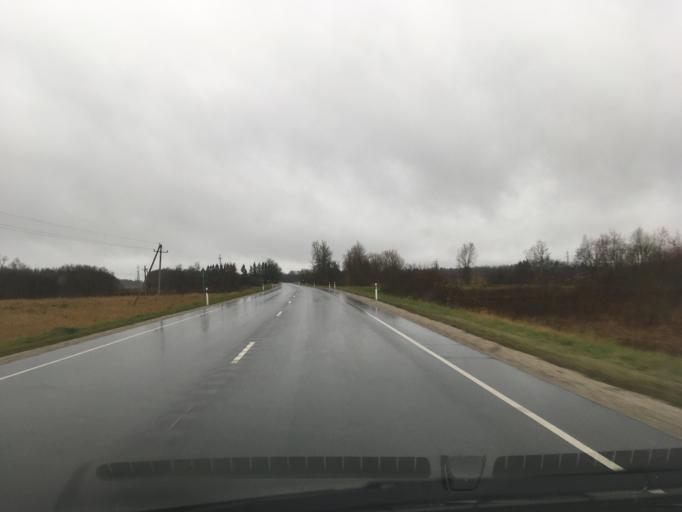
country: EE
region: Laeaene
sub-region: Lihula vald
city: Lihula
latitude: 58.8400
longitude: 24.0578
